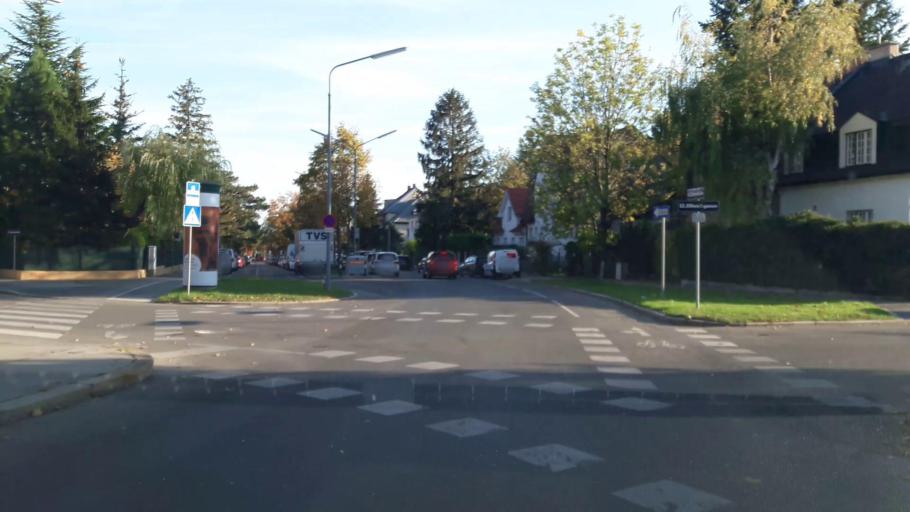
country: AT
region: Lower Austria
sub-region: Politischer Bezirk Modling
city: Perchtoldsdorf
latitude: 48.1719
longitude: 16.3020
